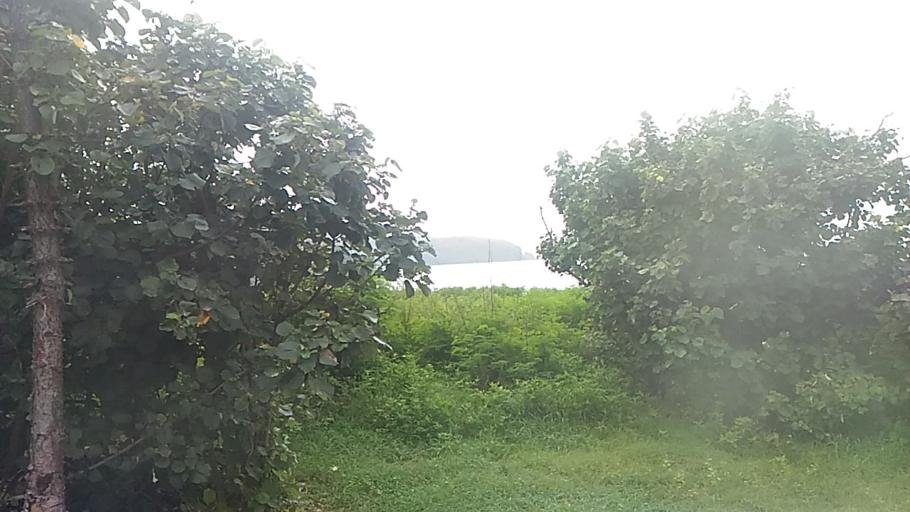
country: TW
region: Taiwan
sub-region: Penghu
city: Ma-kung
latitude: 23.1951
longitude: 119.4286
